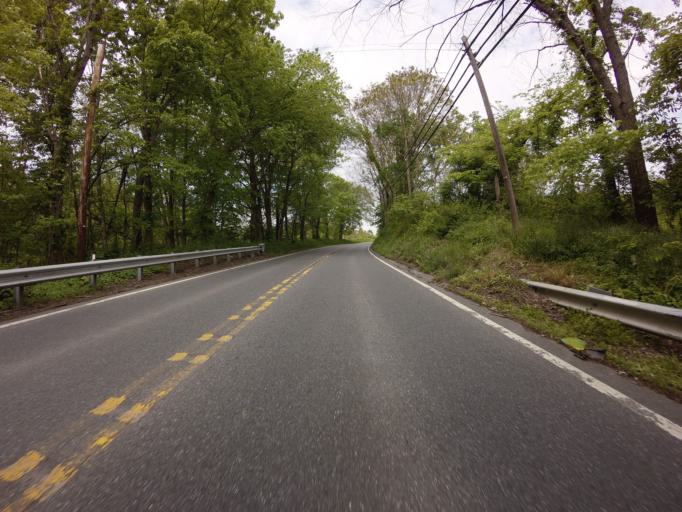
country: US
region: Maryland
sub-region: Frederick County
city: Urbana
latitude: 39.3184
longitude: -77.3344
